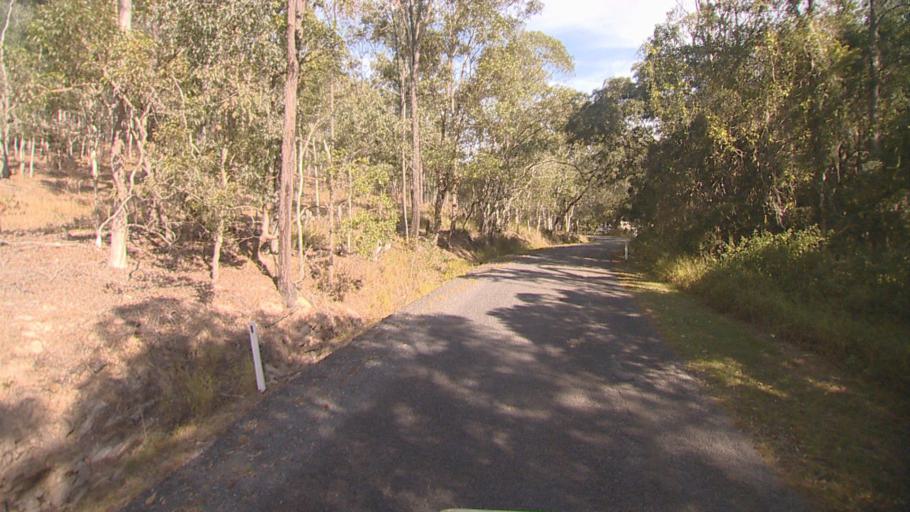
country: AU
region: Queensland
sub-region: Logan
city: Windaroo
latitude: -27.7767
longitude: 153.1747
